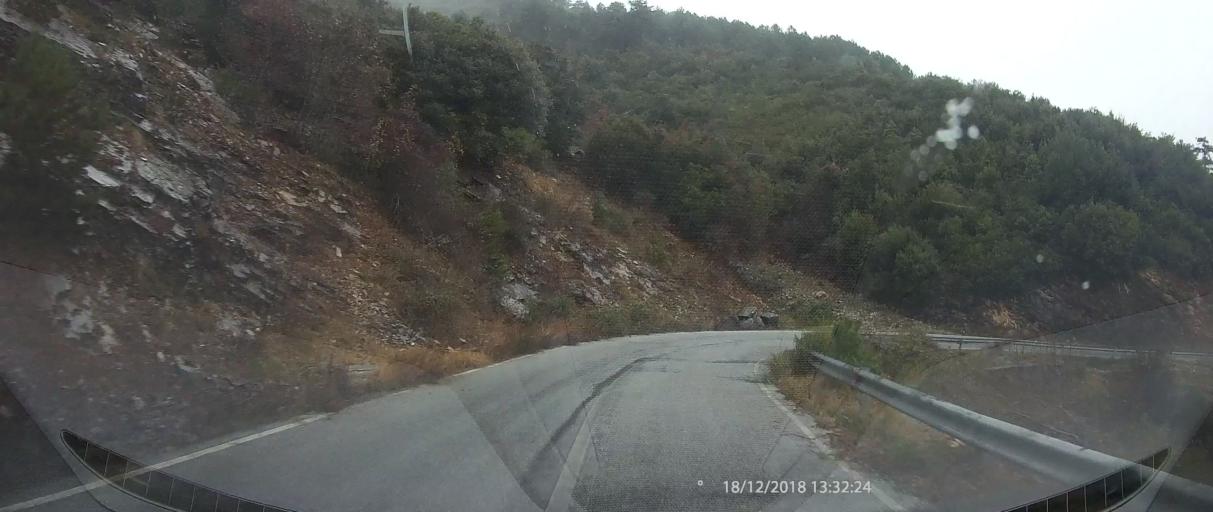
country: GR
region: Central Macedonia
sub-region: Nomos Pierias
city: Litochoro
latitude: 40.1149
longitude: 22.4793
